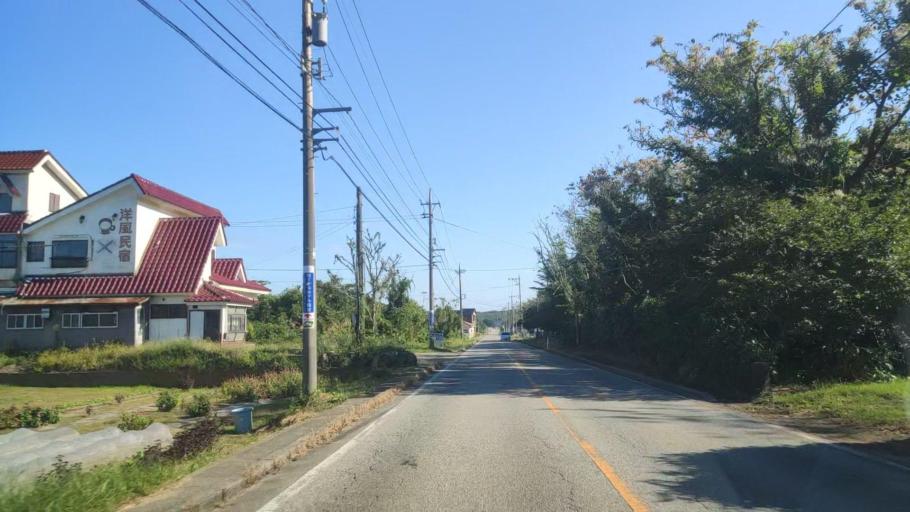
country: JP
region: Ishikawa
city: Hakui
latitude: 36.9554
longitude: 136.7691
